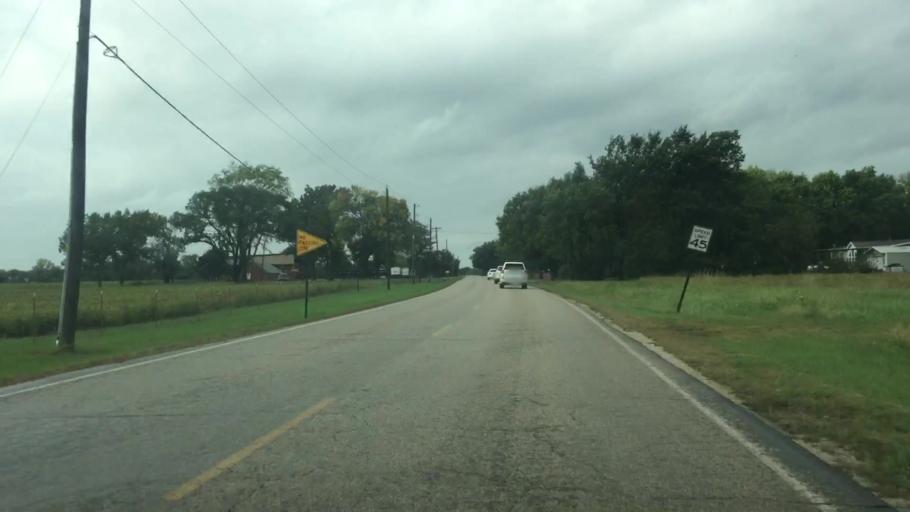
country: US
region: Kansas
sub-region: Allen County
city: Iola
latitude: 37.8857
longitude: -95.4187
